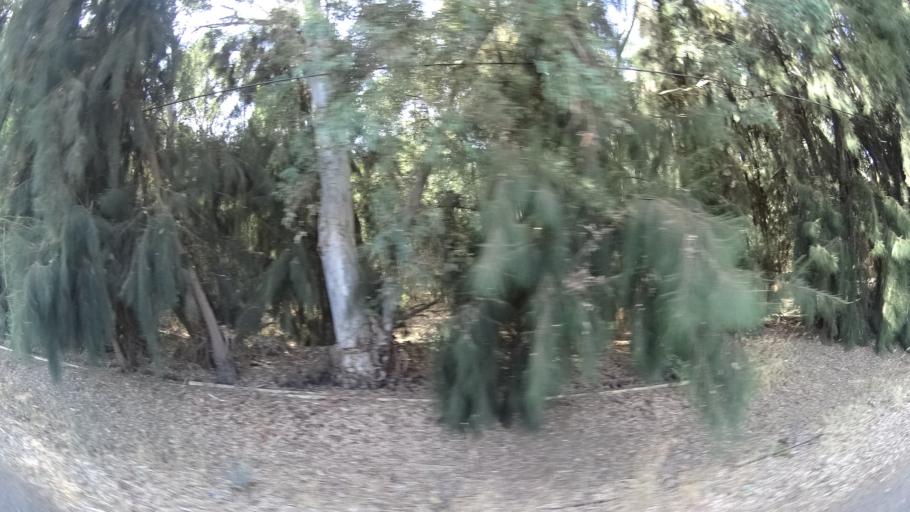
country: US
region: California
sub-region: Yolo County
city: Woodland
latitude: 38.7258
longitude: -121.8564
